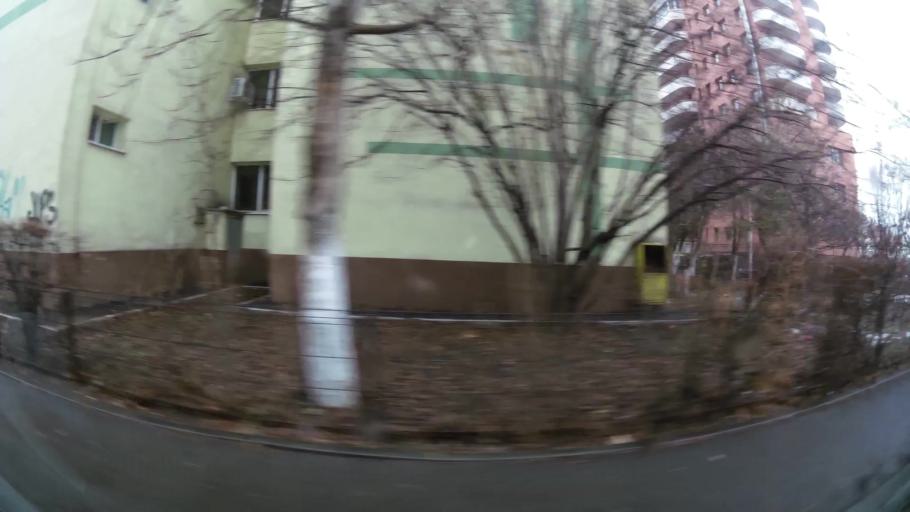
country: RO
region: Ilfov
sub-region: Comuna Chiajna
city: Rosu
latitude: 44.4821
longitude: 26.0578
